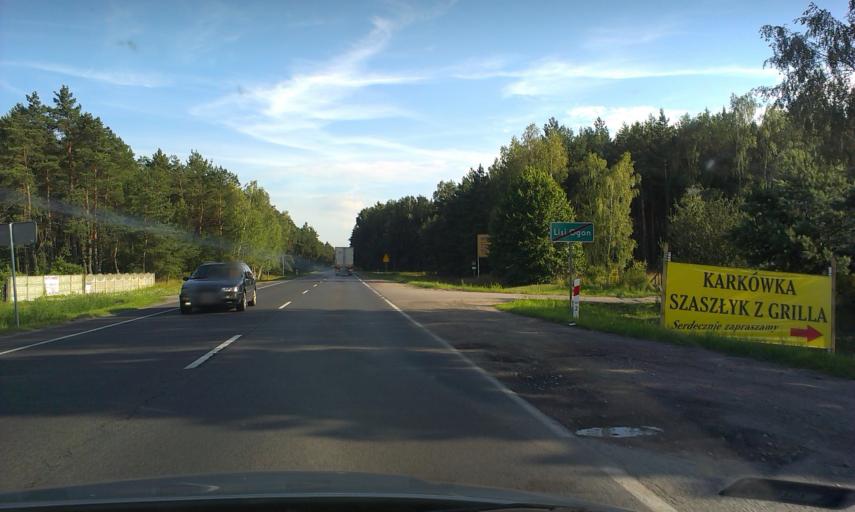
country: PL
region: Kujawsko-Pomorskie
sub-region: Powiat bydgoski
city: Biale Blota
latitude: 53.1216
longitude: 17.8821
